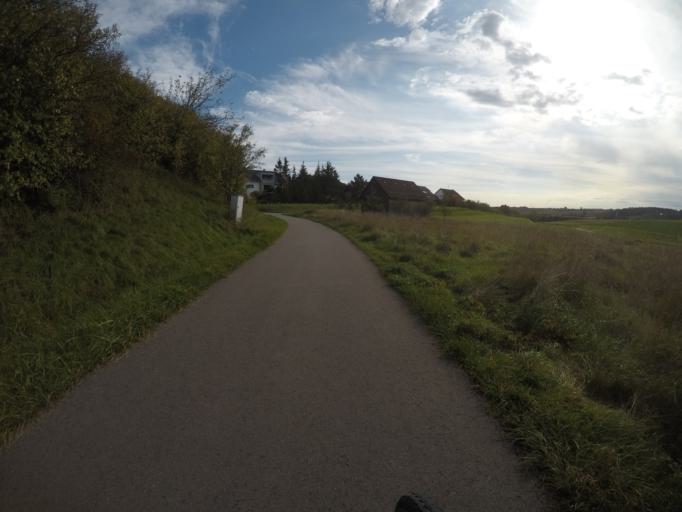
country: DE
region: Baden-Wuerttemberg
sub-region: Regierungsbezirk Stuttgart
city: Herrenberg
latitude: 48.5793
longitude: 8.8742
